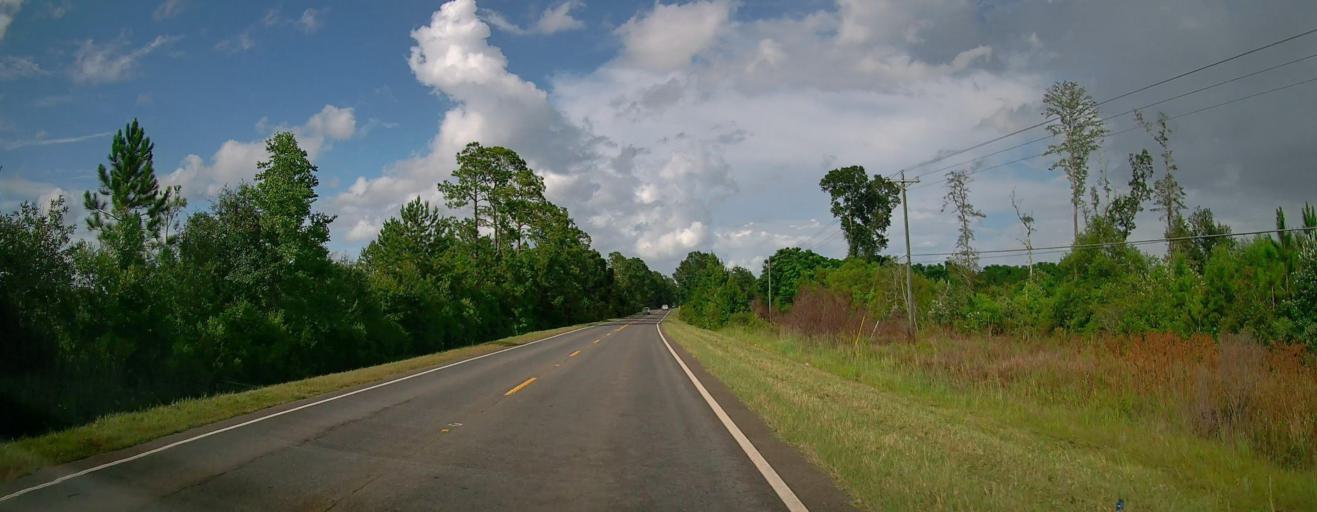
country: US
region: Georgia
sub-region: Coffee County
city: Douglas
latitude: 31.4699
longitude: -82.8785
